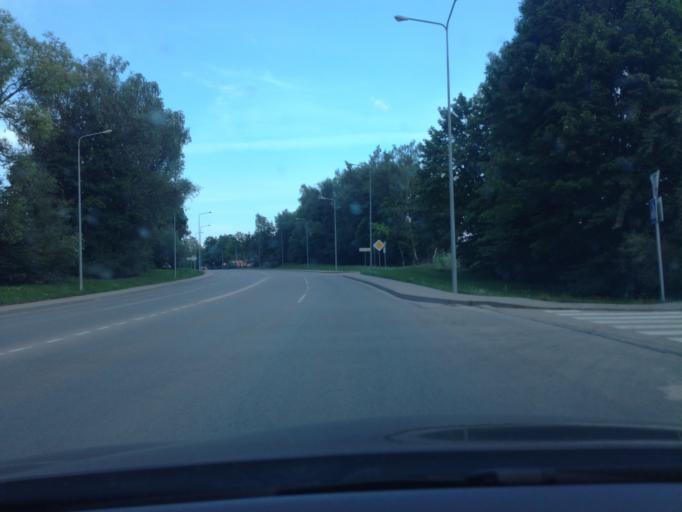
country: LT
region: Alytaus apskritis
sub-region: Alytus
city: Alytus
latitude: 54.3923
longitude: 24.0003
